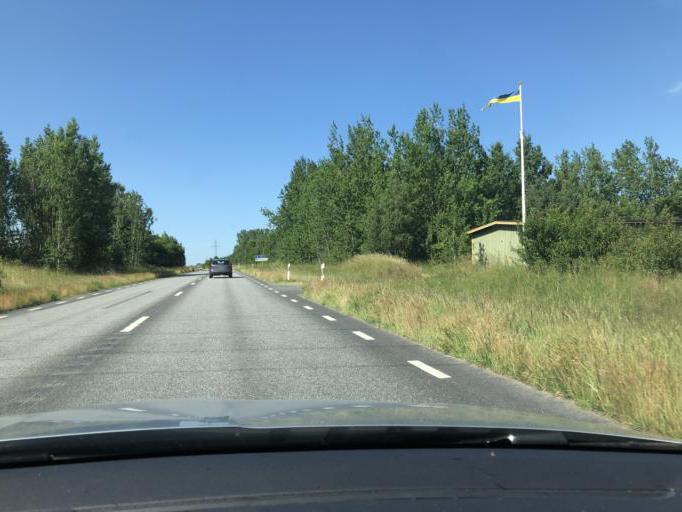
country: SE
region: Skane
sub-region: Bromolla Kommun
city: Bromoella
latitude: 56.0726
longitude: 14.4989
